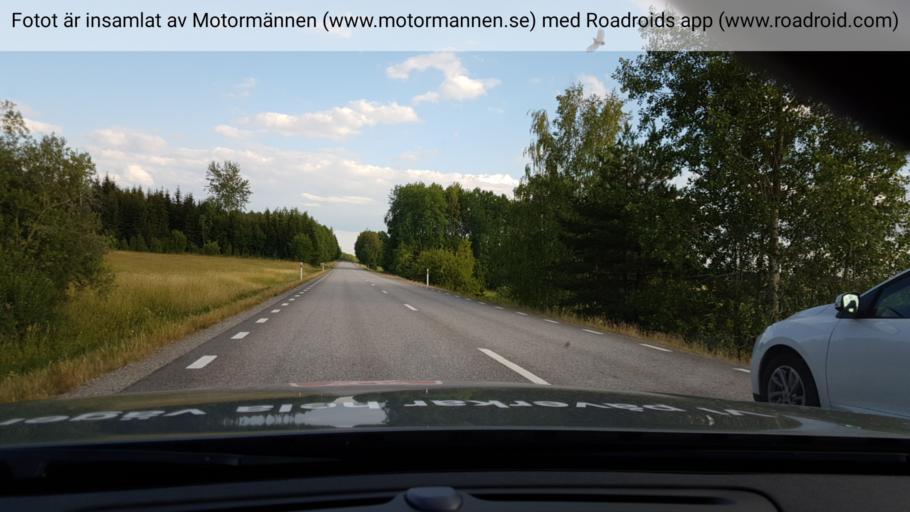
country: SE
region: Uppsala
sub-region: Heby Kommun
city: Heby
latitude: 59.9101
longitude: 16.8912
